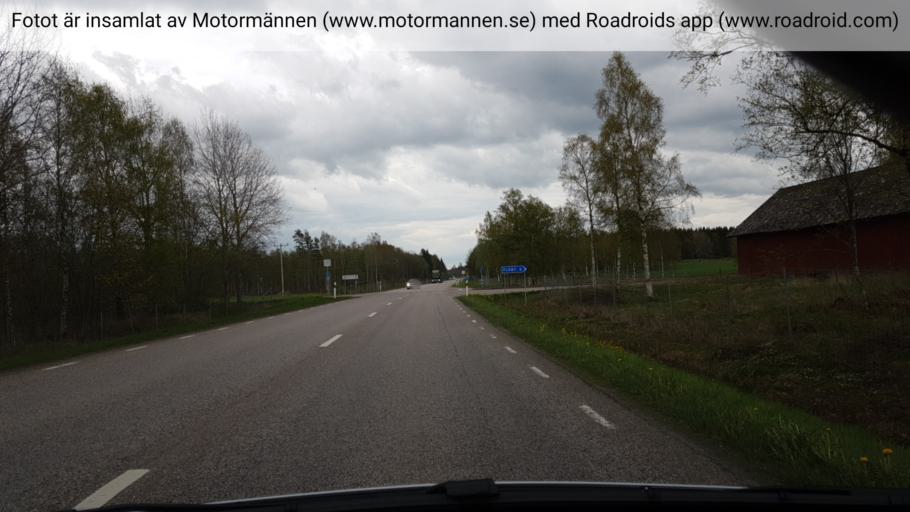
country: SE
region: Vaestra Goetaland
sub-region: Falkopings Kommun
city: Floby
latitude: 58.1892
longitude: 13.3502
